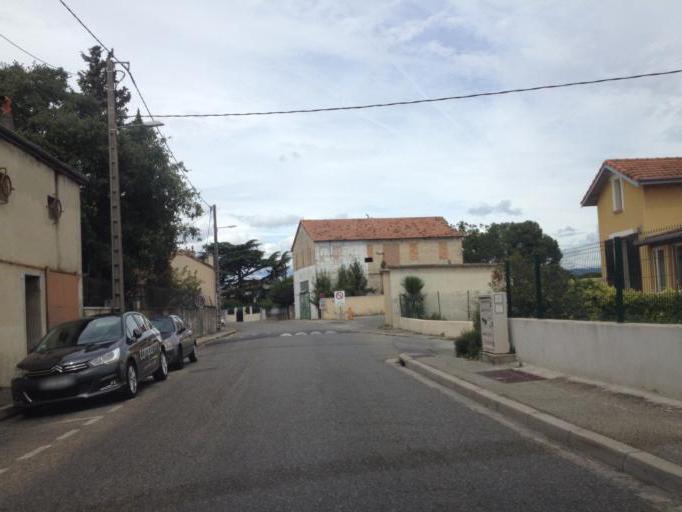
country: FR
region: Rhone-Alpes
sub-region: Departement de la Drome
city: Montelimar
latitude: 44.5487
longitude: 4.7525
